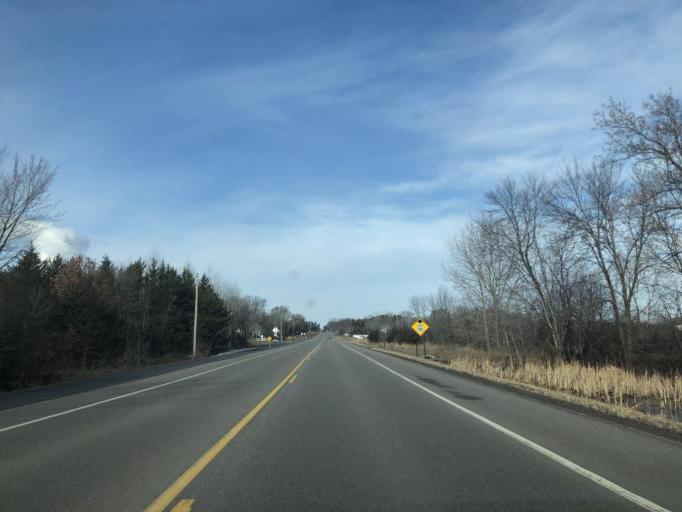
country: US
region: Minnesota
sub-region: Sherburne County
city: Becker
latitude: 45.3937
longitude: -93.8563
